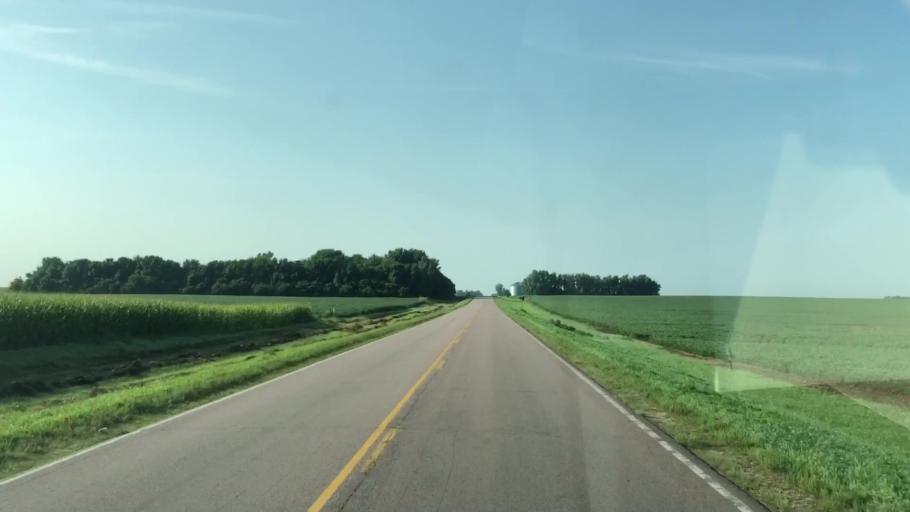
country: US
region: Iowa
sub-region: Lyon County
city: George
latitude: 43.3252
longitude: -95.9988
